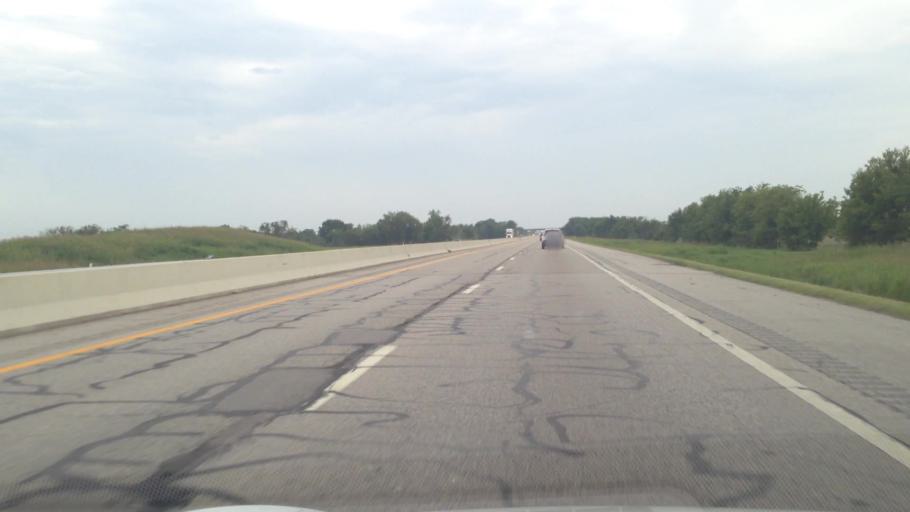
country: US
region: Oklahoma
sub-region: Ottawa County
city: Fairland
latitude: 36.7792
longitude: -94.8906
